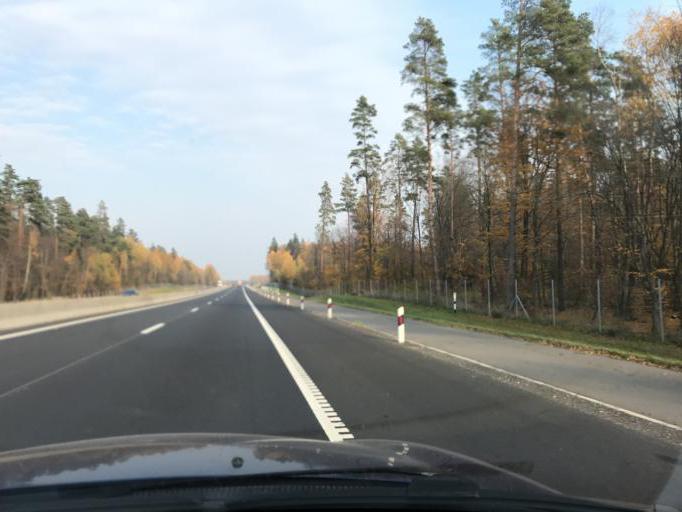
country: BY
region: Grodnenskaya
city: Shchuchin
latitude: 53.6714
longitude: 24.8316
